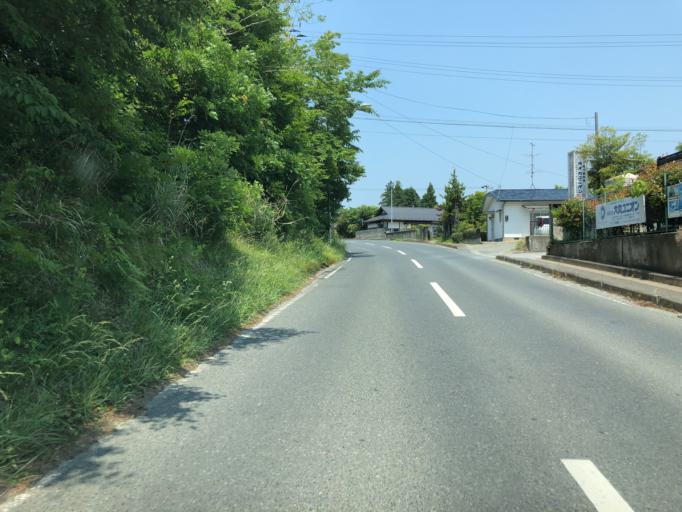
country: JP
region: Miyagi
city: Marumori
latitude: 37.8194
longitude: 140.8962
